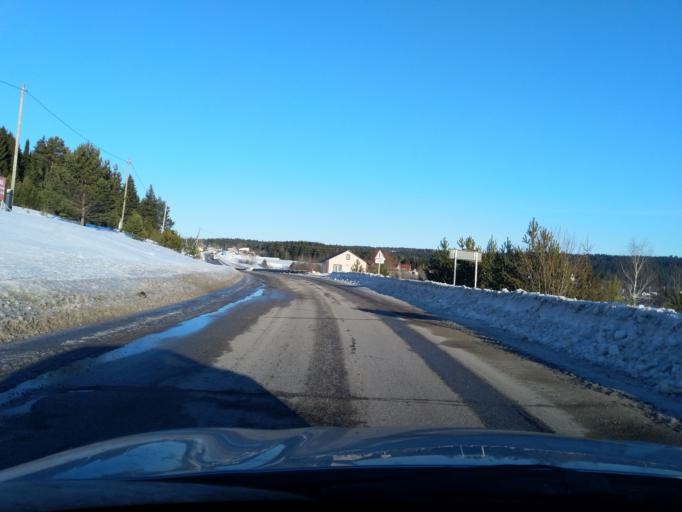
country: RU
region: Perm
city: Polazna
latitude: 58.3058
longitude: 56.4442
